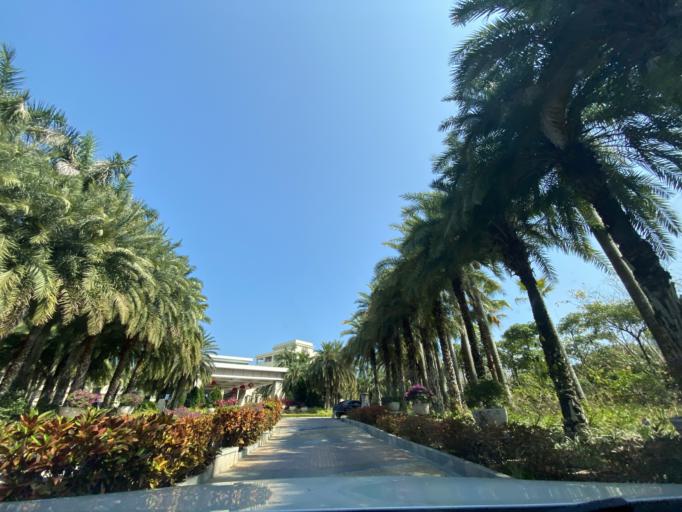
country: CN
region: Hainan
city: Haitangwan
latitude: 18.3483
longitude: 109.7353
